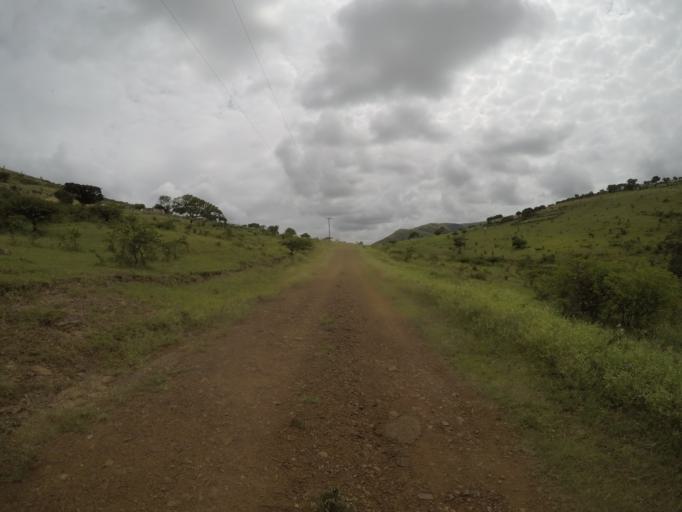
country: ZA
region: KwaZulu-Natal
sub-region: uThungulu District Municipality
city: Empangeni
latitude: -28.6201
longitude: 31.8915
